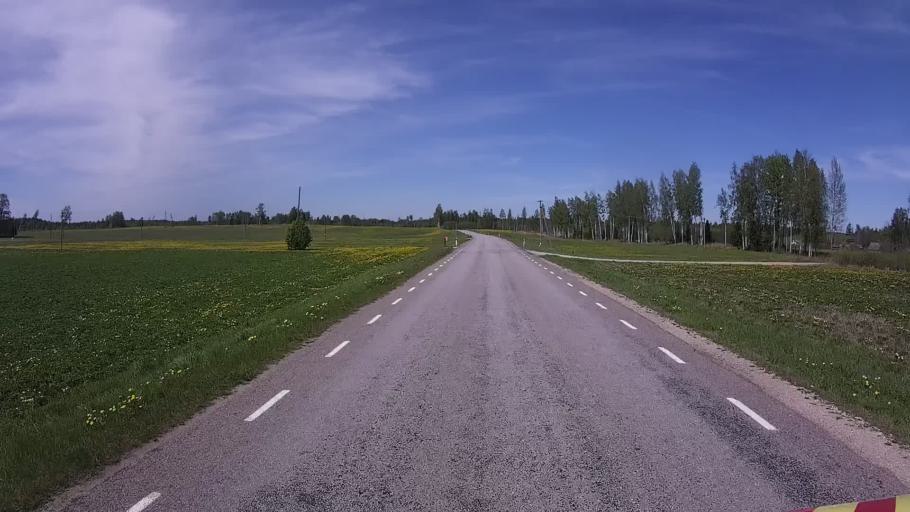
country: EE
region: Vorumaa
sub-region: Antsla vald
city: Vana-Antsla
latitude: 57.6346
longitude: 26.3384
